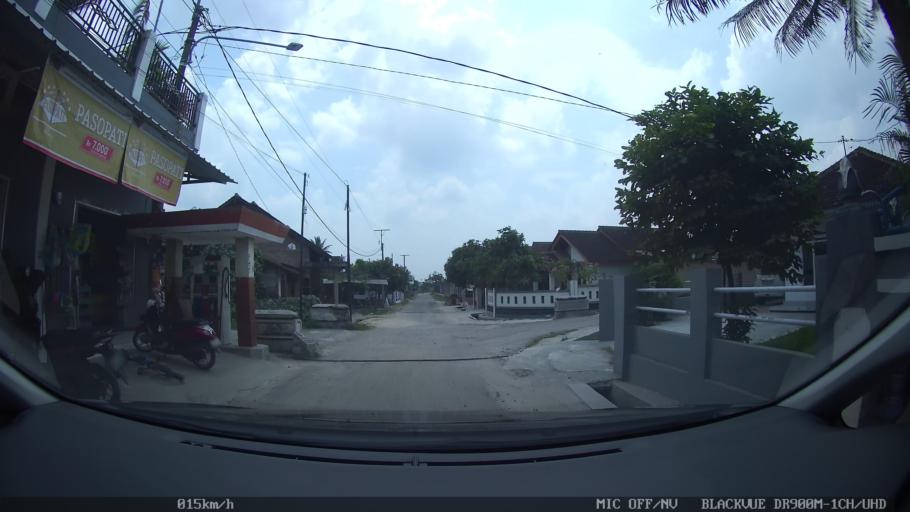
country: ID
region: Lampung
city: Pringsewu
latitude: -5.3472
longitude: 104.9883
